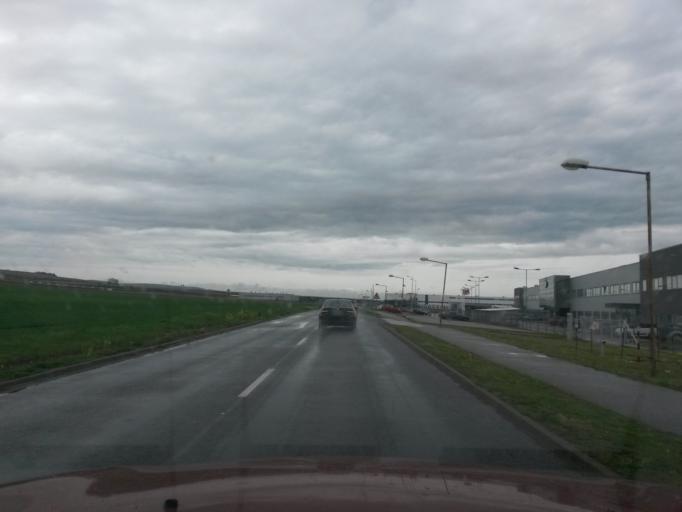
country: HU
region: Borsod-Abauj-Zemplen
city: Gonc
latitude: 48.5504
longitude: 21.2448
